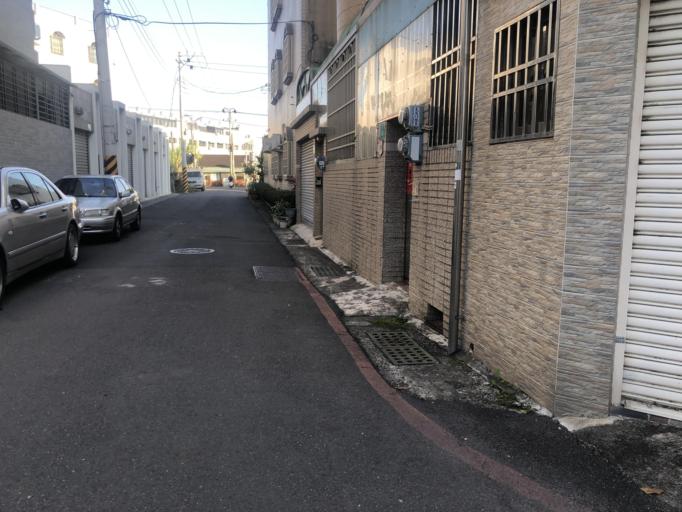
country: TW
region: Taiwan
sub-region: Tainan
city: Tainan
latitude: 23.0383
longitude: 120.1840
